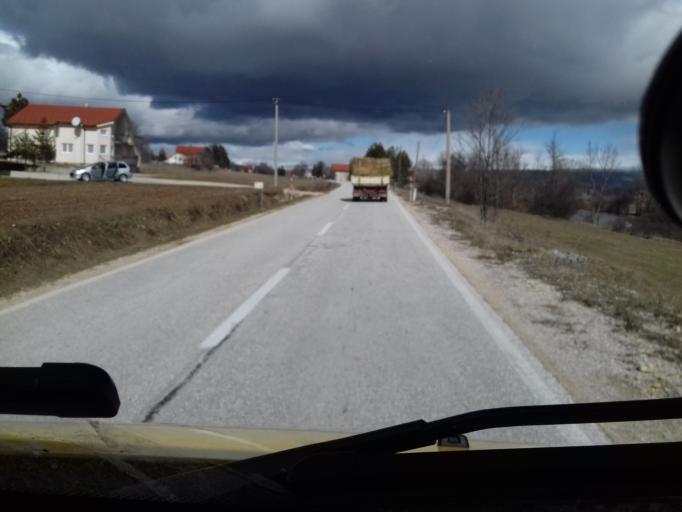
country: BA
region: Federation of Bosnia and Herzegovina
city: Dreznica
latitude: 43.5991
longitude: 17.2740
